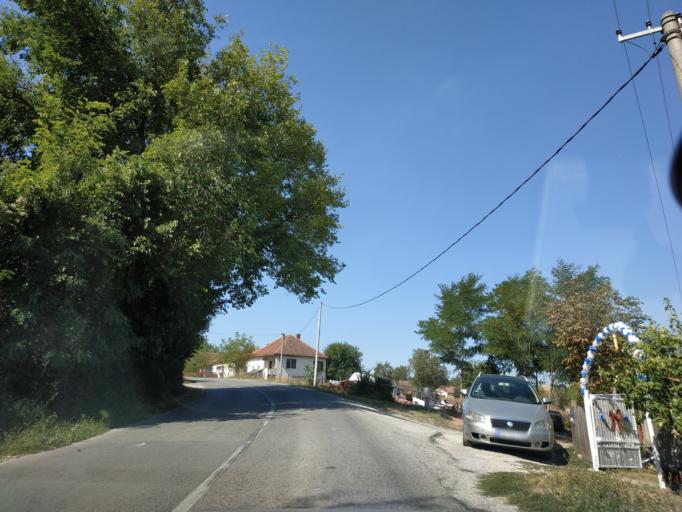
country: RS
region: Central Serbia
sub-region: Sumadijski Okrug
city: Arangelovac
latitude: 44.2813
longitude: 20.6193
